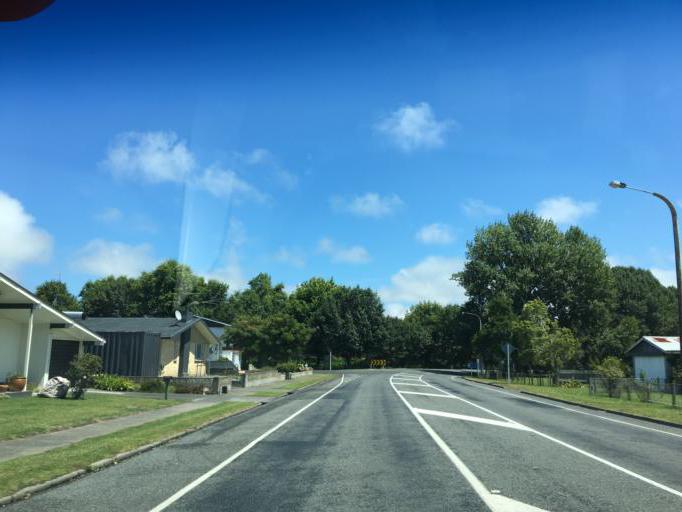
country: NZ
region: Hawke's Bay
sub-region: Wairoa District
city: Wairoa
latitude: -39.0373
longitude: 177.4152
